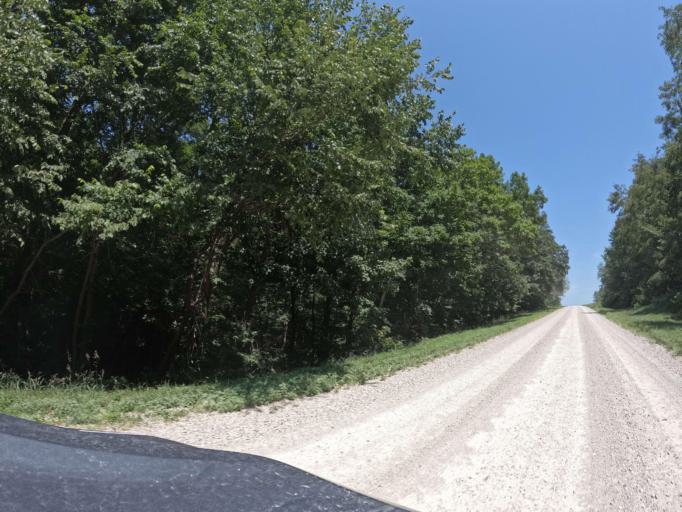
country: US
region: Iowa
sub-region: Henry County
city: Mount Pleasant
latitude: 40.9449
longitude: -91.6753
